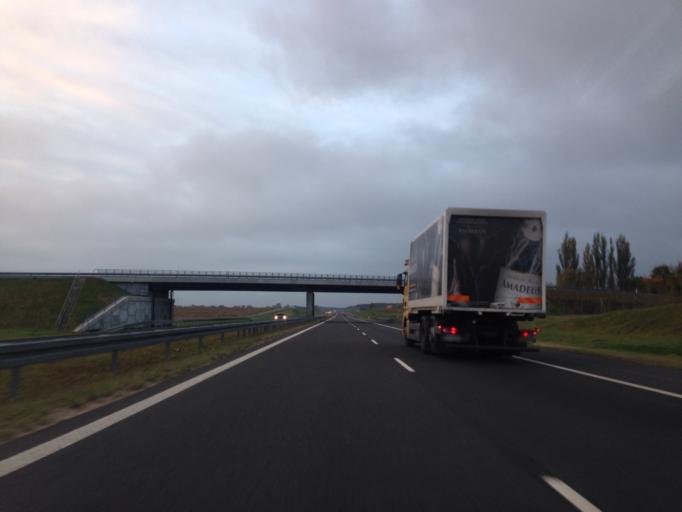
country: PL
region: Kujawsko-Pomorskie
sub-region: Powiat swiecki
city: Warlubie
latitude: 53.5967
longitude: 18.6164
